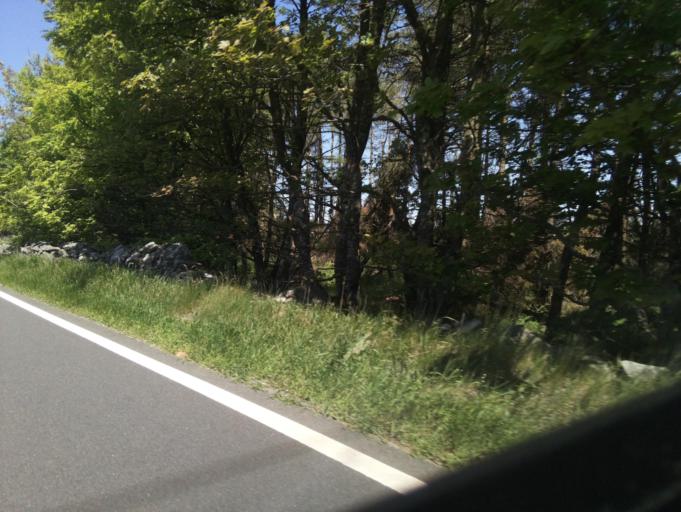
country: GB
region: Scotland
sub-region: The Scottish Borders
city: Hawick
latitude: 55.4697
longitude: -2.7922
